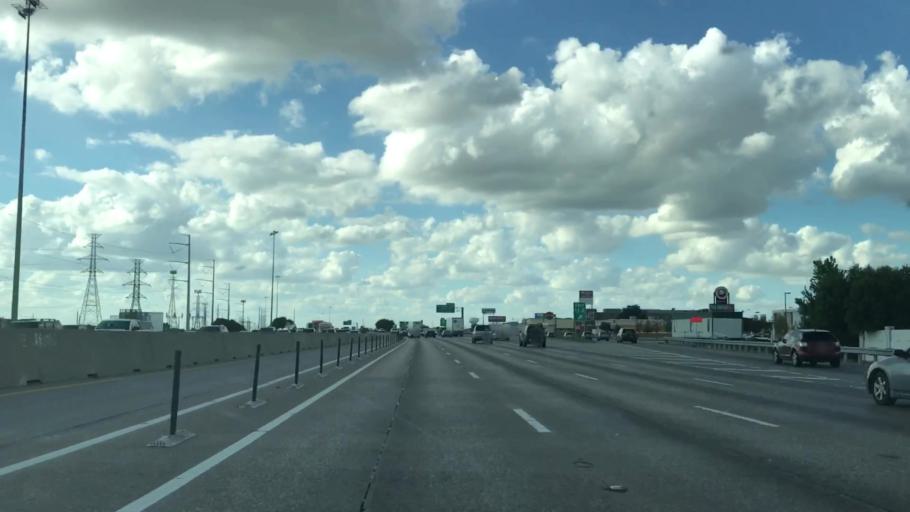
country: US
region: Texas
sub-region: Dallas County
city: Garland
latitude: 32.8527
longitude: -96.6442
